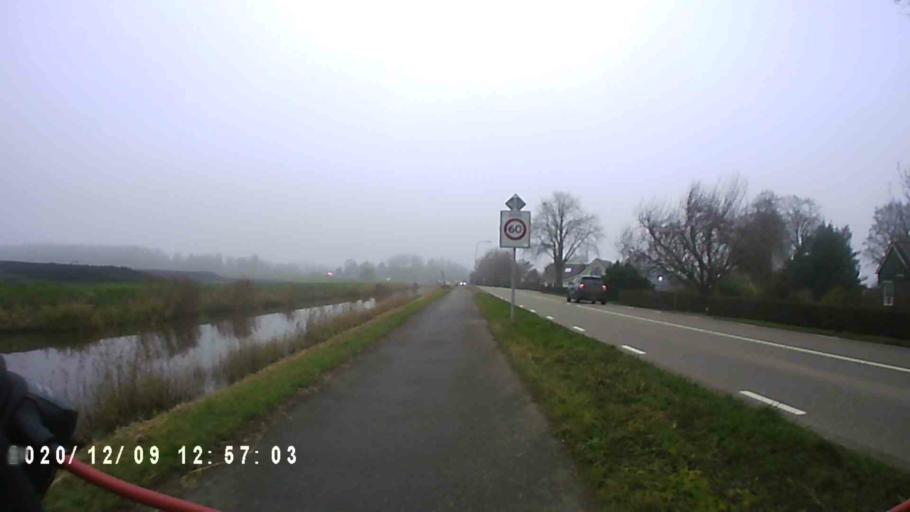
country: NL
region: Groningen
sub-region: Gemeente Groningen
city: Oosterpark
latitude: 53.2284
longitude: 6.6414
